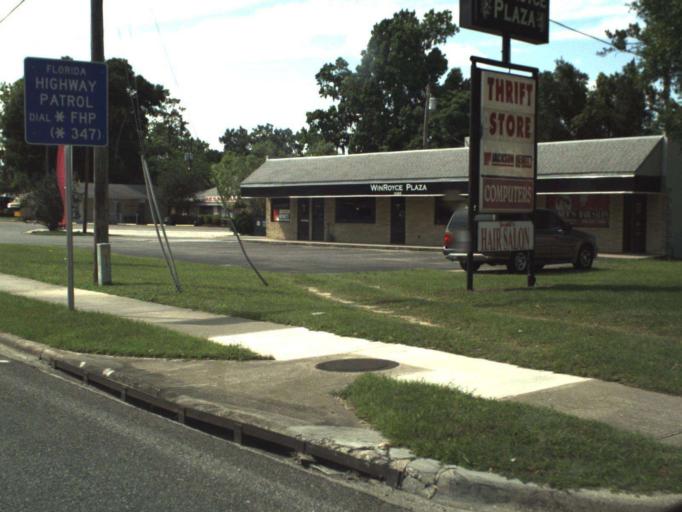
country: US
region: Florida
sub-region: Marion County
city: Belleview
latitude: 29.0610
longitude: -82.0642
